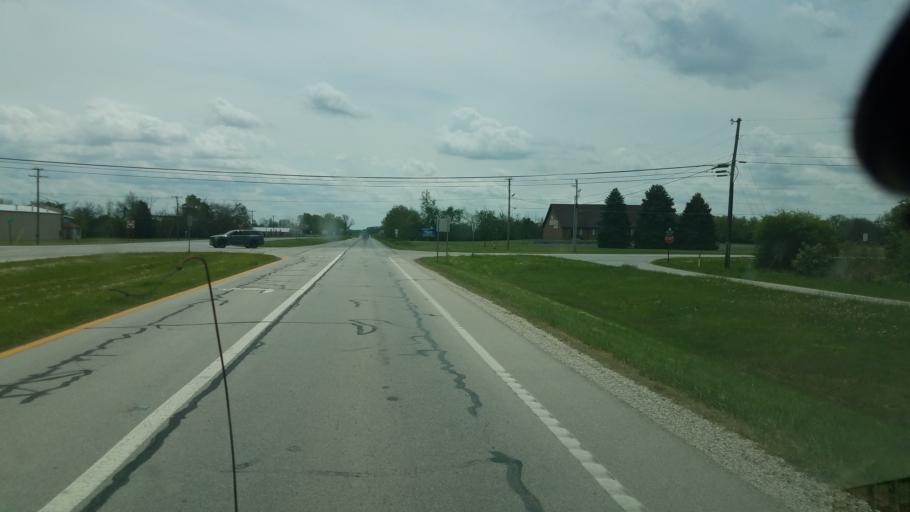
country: US
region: Ohio
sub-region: Sandusky County
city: Stony Prairie
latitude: 41.3286
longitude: -83.1680
